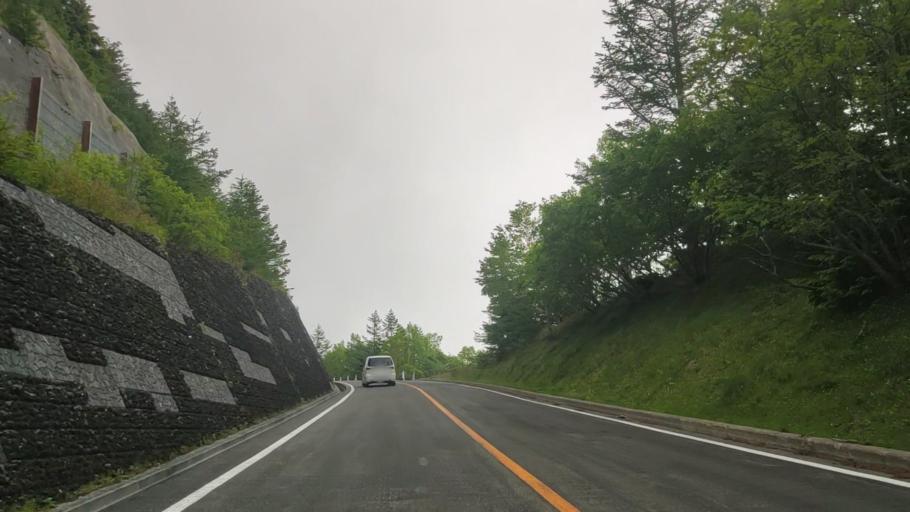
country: JP
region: Yamanashi
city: Fujikawaguchiko
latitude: 35.3845
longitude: 138.6975
